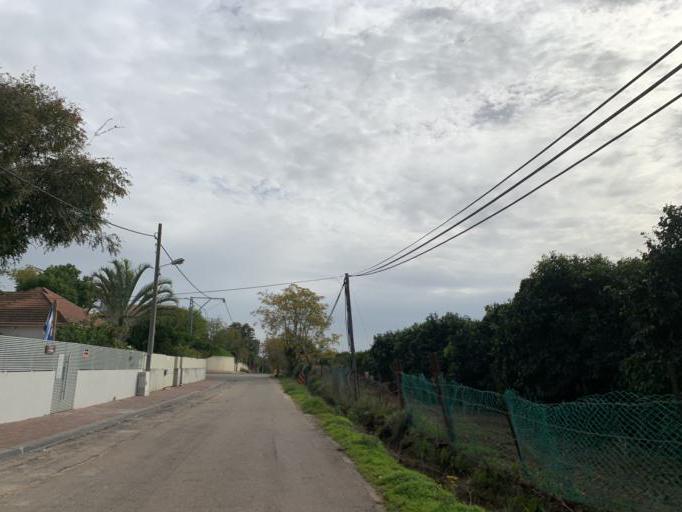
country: IL
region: Central District
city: Hod HaSharon
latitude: 32.1498
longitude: 34.9018
